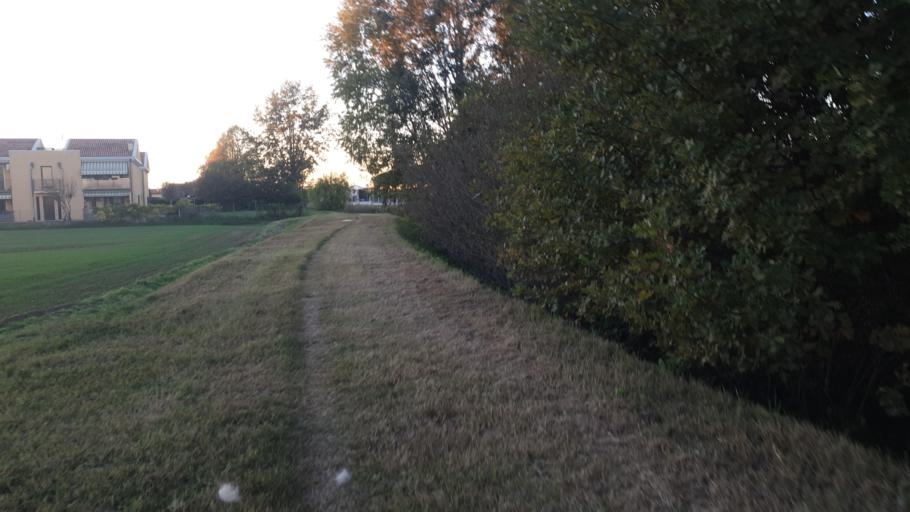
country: IT
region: Veneto
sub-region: Provincia di Venezia
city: Cazzago-Ex Polo
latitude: 45.4439
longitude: 12.0782
